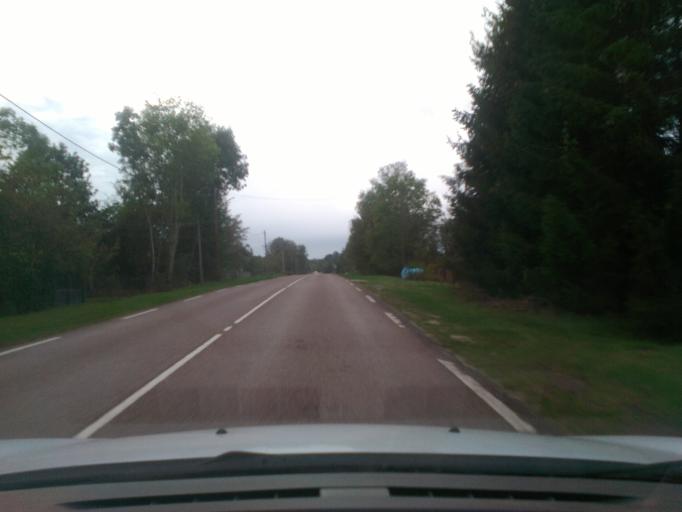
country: FR
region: Lorraine
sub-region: Departement des Vosges
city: Chatel-sur-Moselle
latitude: 48.3489
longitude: 6.4086
